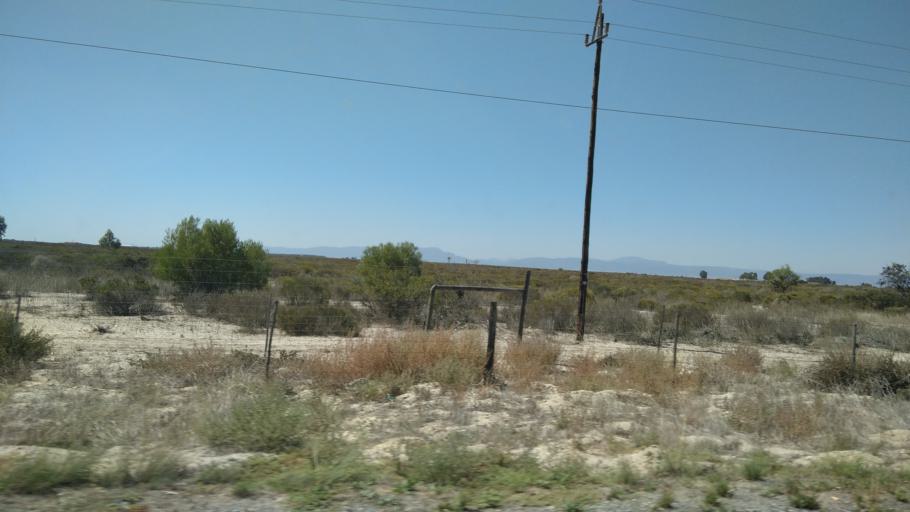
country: ZA
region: Western Cape
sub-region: West Coast District Municipality
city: Vredenburg
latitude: -33.0330
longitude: 18.2930
